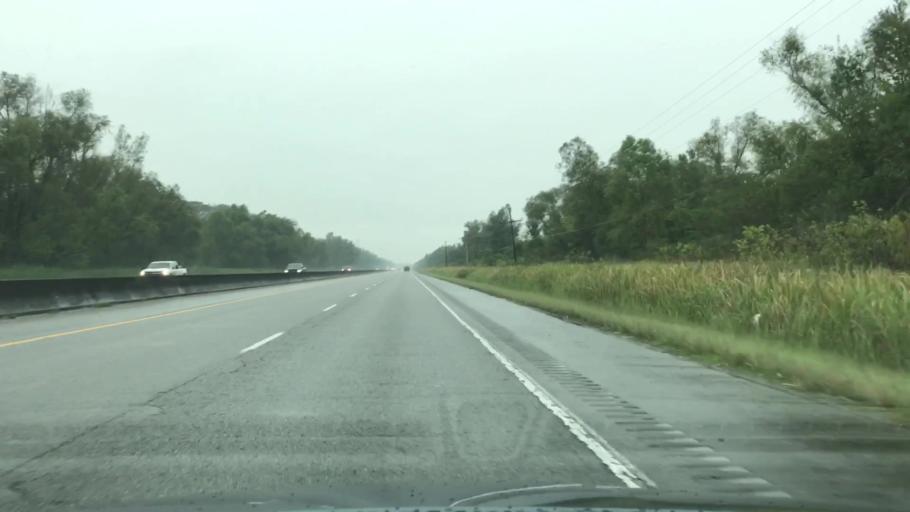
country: US
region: Louisiana
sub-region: Saint Charles Parish
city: Des Allemands
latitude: 29.7758
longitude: -90.5323
